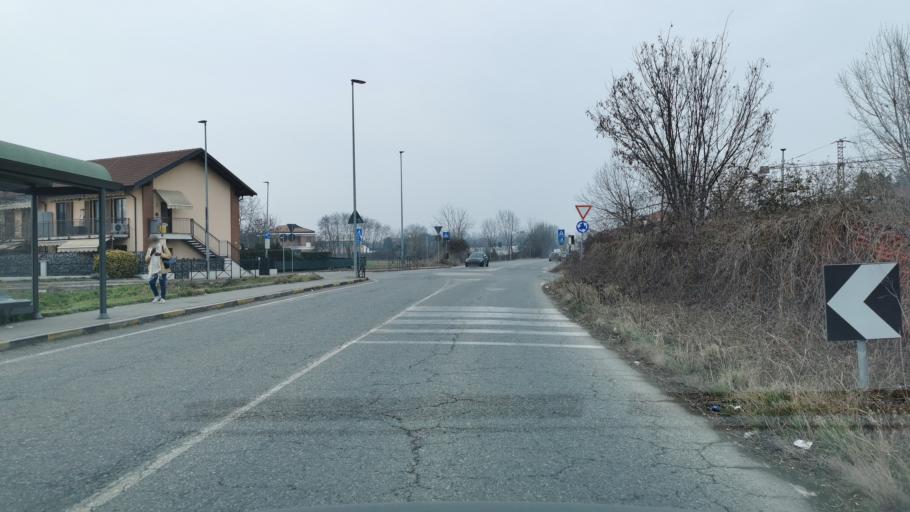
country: IT
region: Piedmont
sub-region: Provincia di Torino
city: Borgaro Torinese
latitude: 45.1313
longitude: 7.6870
